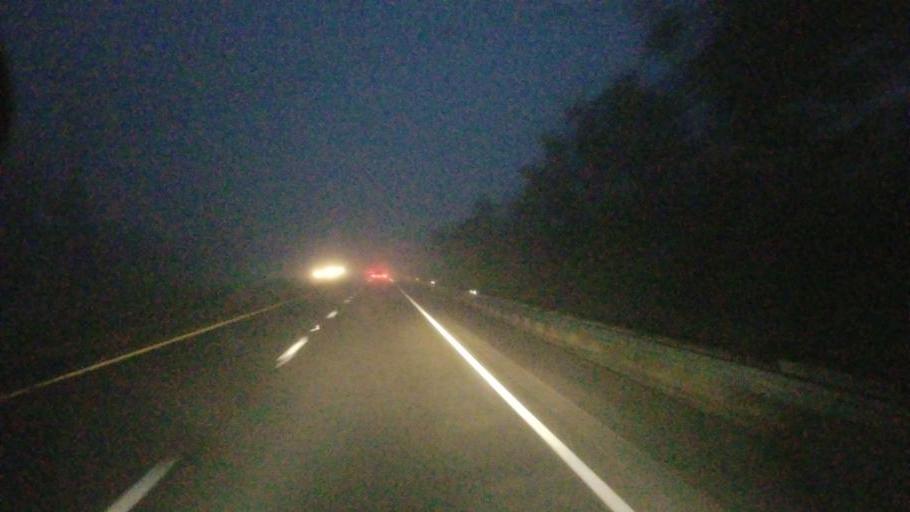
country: US
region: Ohio
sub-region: Ross County
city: Chillicothe
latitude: 39.3709
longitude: -82.9675
